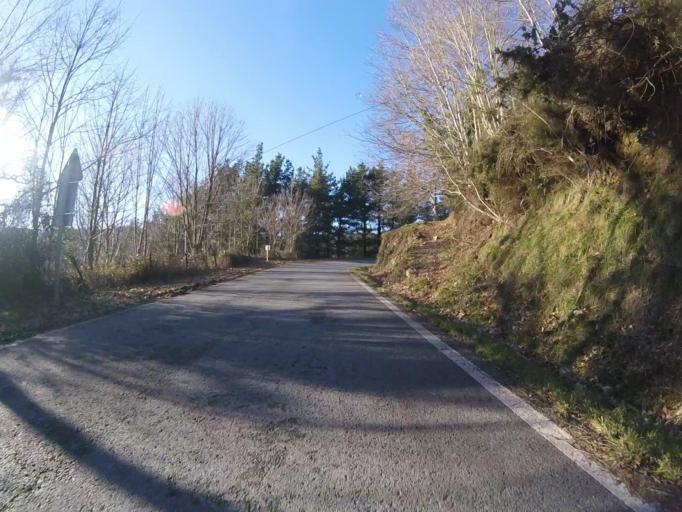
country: ES
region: Navarre
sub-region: Provincia de Navarra
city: Lesaka
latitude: 43.2653
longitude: -1.7408
